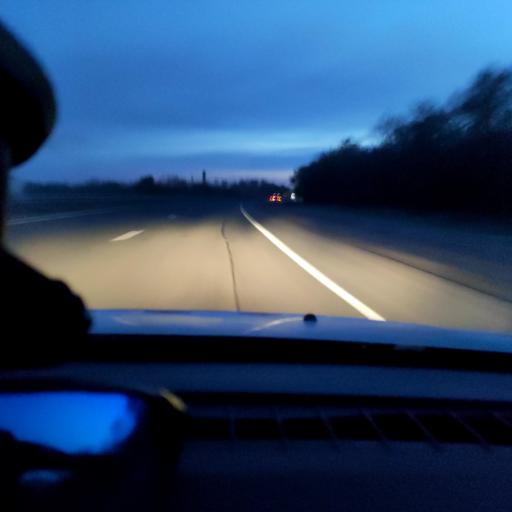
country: RU
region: Samara
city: Novokuybyshevsk
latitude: 53.0497
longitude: 50.0090
